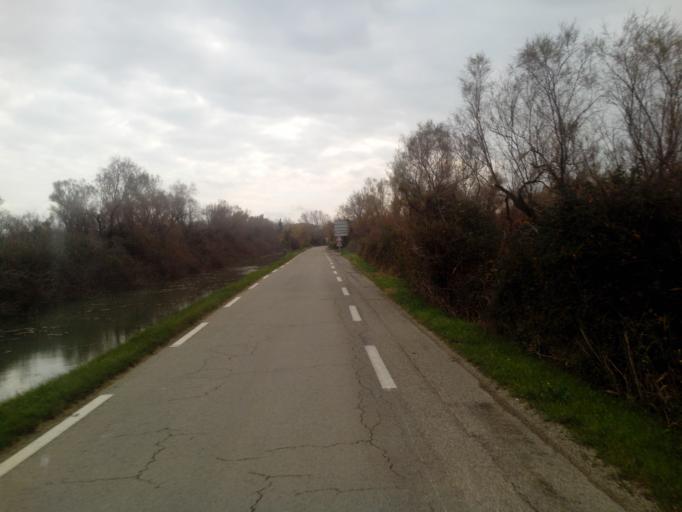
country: FR
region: Languedoc-Roussillon
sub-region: Departement du Gard
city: Vauvert
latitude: 43.6075
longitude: 4.3345
